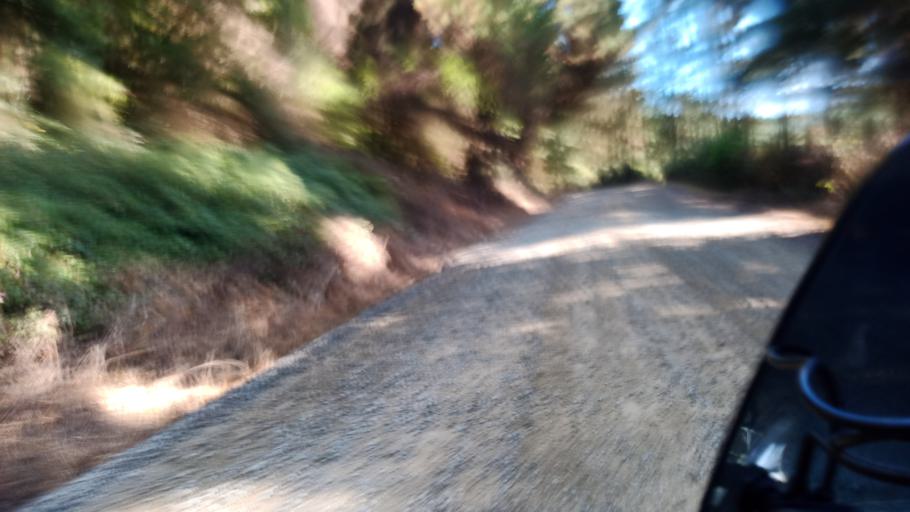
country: NZ
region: Hawke's Bay
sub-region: Wairoa District
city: Wairoa
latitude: -38.9319
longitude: 177.2284
